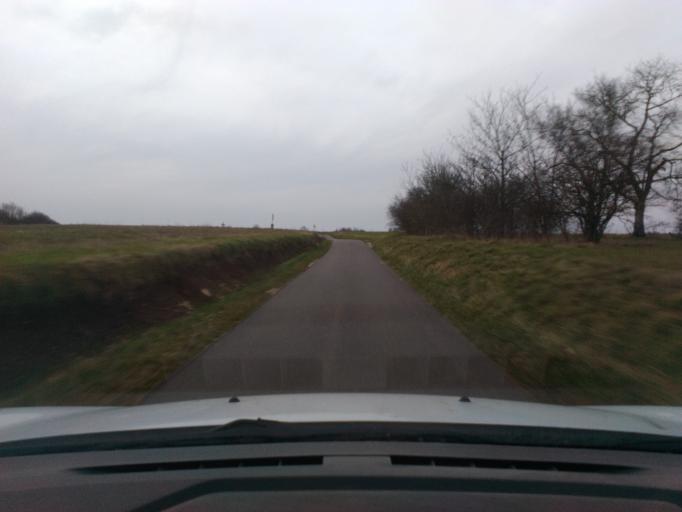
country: FR
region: Lorraine
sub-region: Departement des Vosges
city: Mirecourt
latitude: 48.2831
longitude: 6.1216
